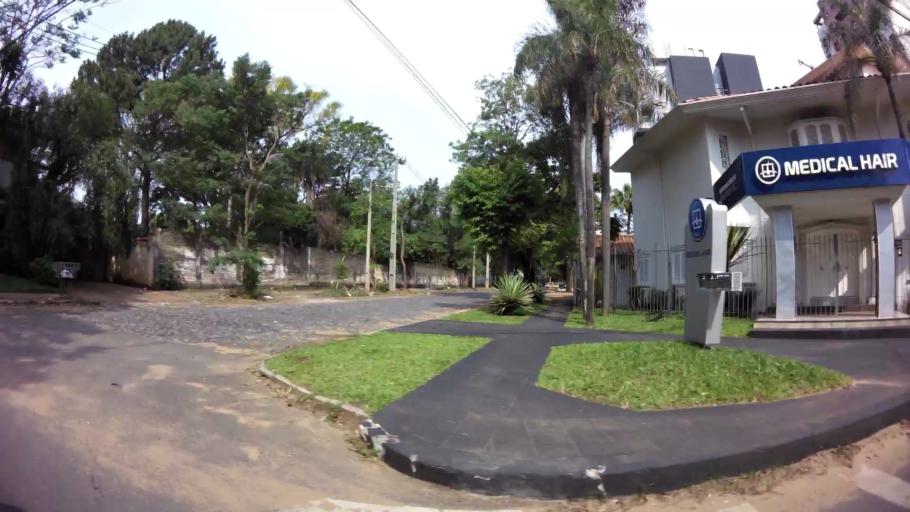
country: PY
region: Central
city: Fernando de la Mora
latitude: -25.2855
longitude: -57.5578
